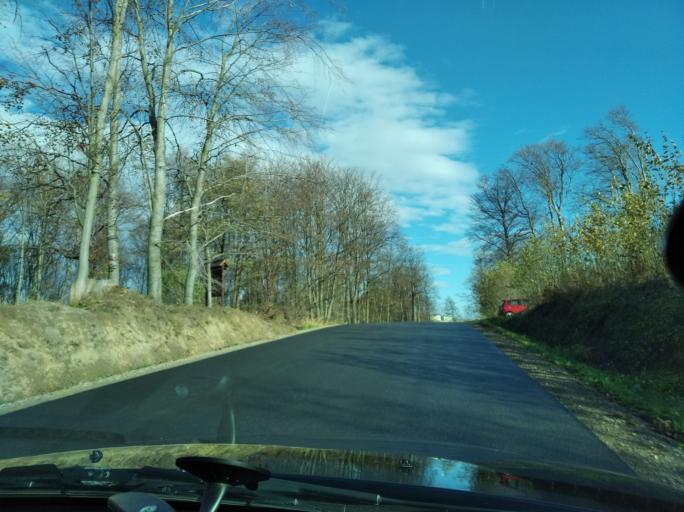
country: PL
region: Subcarpathian Voivodeship
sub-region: Powiat ropczycko-sedziszowski
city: Niedzwiada
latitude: 49.9998
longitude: 21.4622
